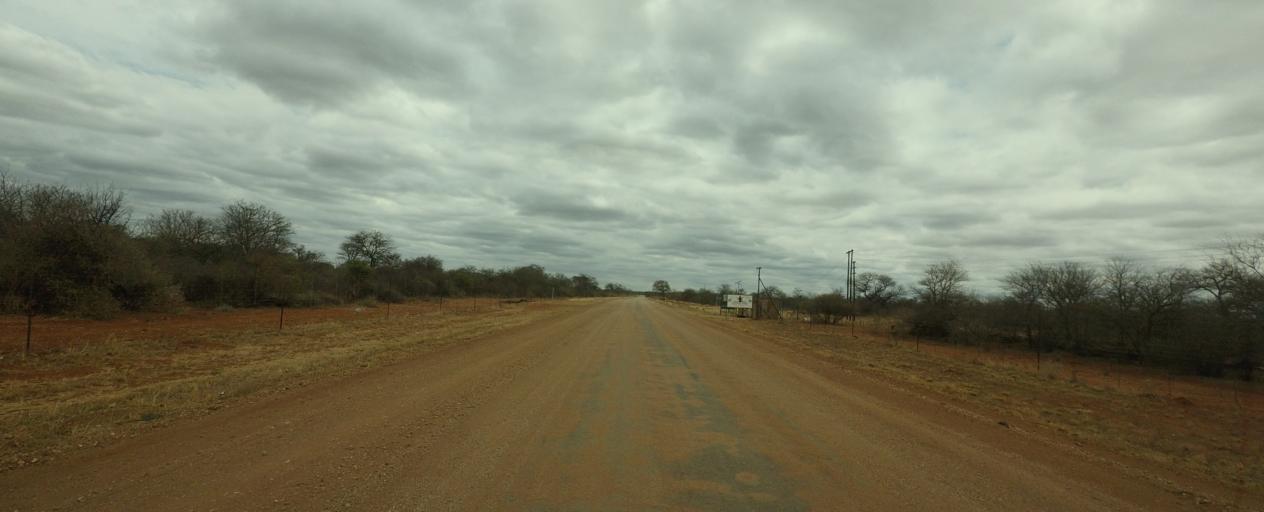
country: BW
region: Central
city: Mathathane
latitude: -22.7091
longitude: 28.5800
